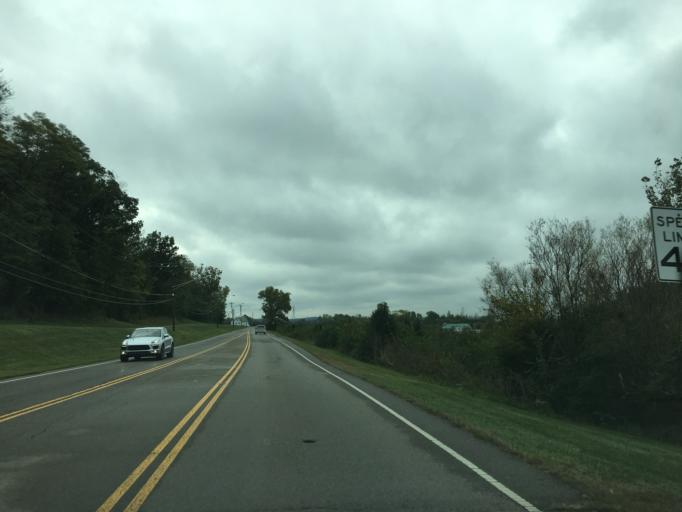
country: US
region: Ohio
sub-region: Butler County
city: Beckett Ridge
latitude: 39.3486
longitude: -84.4488
